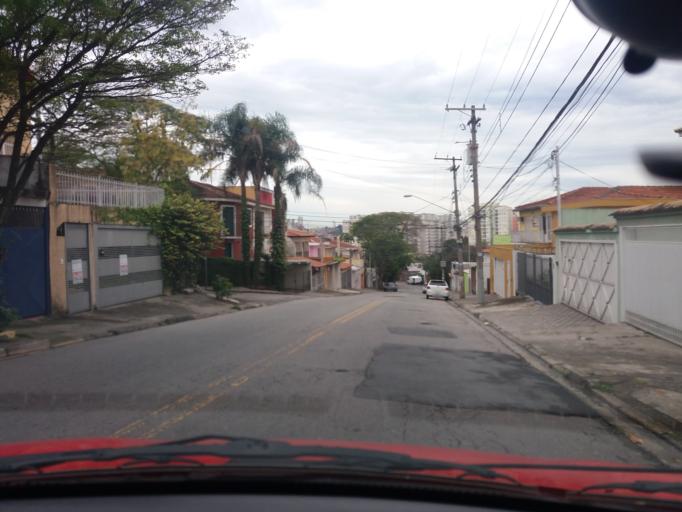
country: BR
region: Sao Paulo
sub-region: Taboao Da Serra
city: Taboao da Serra
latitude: -23.5821
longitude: -46.7403
